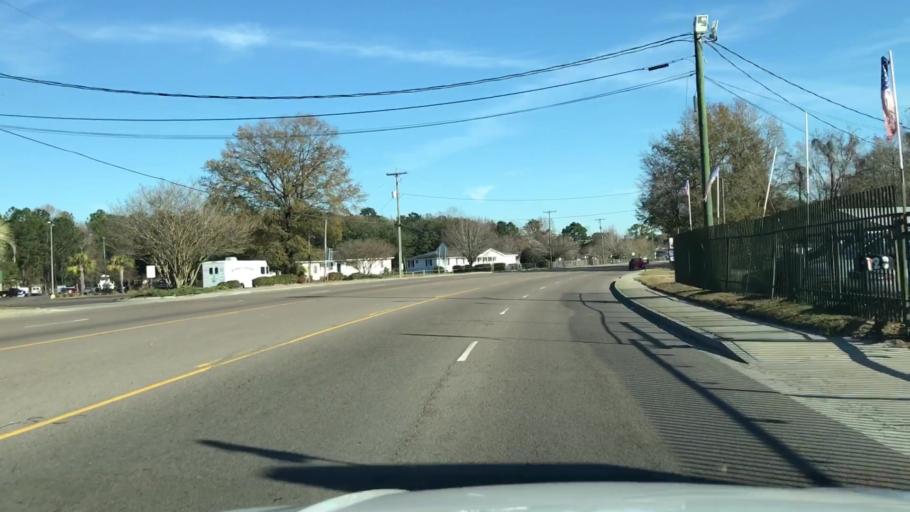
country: US
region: South Carolina
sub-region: Berkeley County
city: Ladson
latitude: 32.9912
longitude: -80.1004
